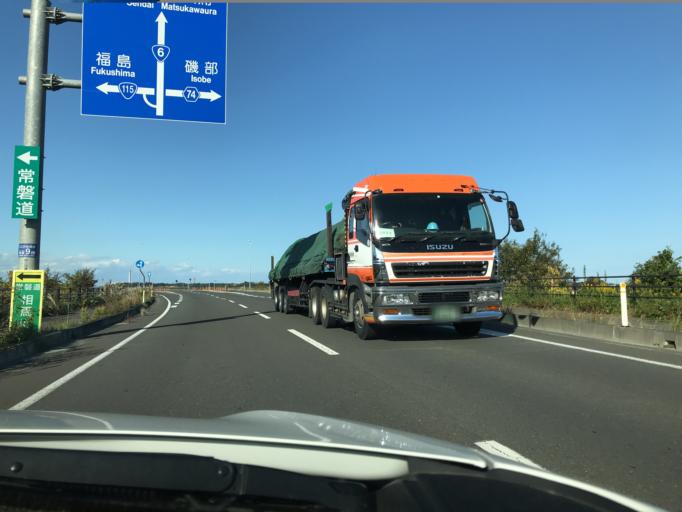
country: JP
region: Miyagi
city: Marumori
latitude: 37.7871
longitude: 140.9439
